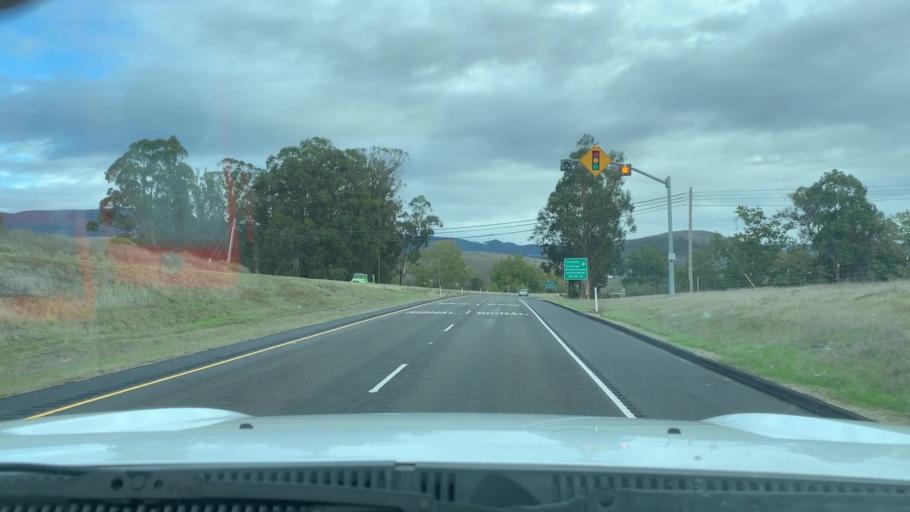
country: US
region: California
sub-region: San Luis Obispo County
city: Los Osos
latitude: 35.3331
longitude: -120.7467
